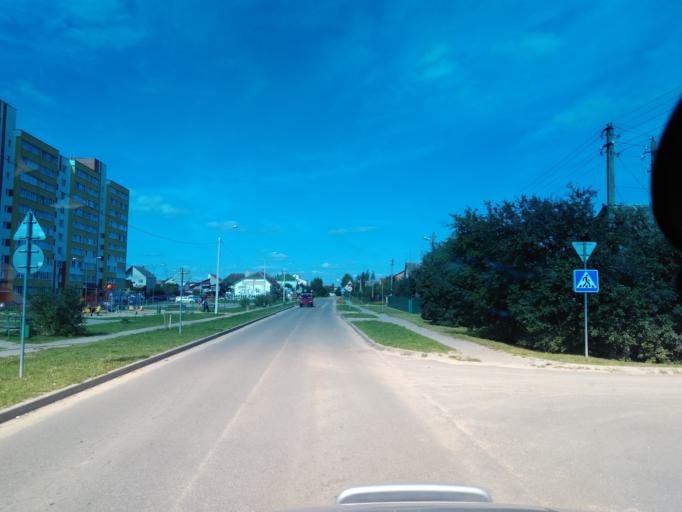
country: BY
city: Fanipol
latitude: 53.7515
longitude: 27.3356
